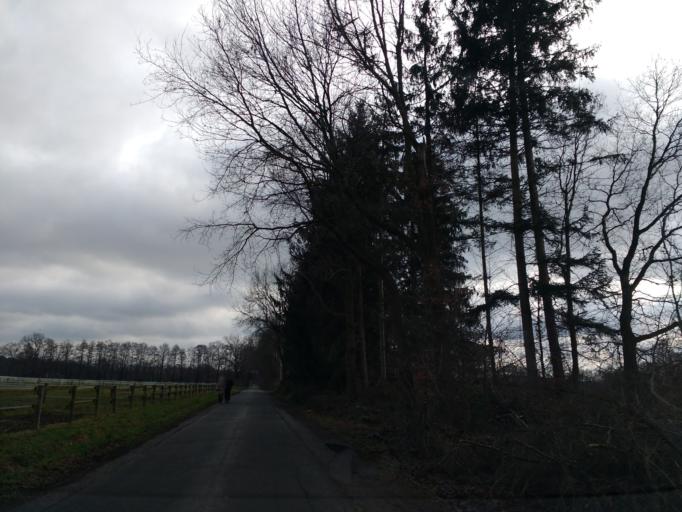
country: DE
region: North Rhine-Westphalia
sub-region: Regierungsbezirk Detmold
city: Hovelhof
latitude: 51.8271
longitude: 8.6882
